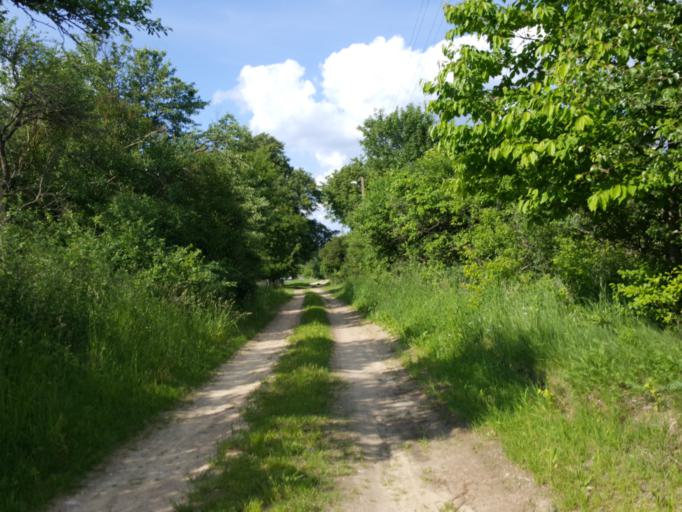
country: BY
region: Brest
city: Vysokaye
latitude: 52.4393
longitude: 23.5759
